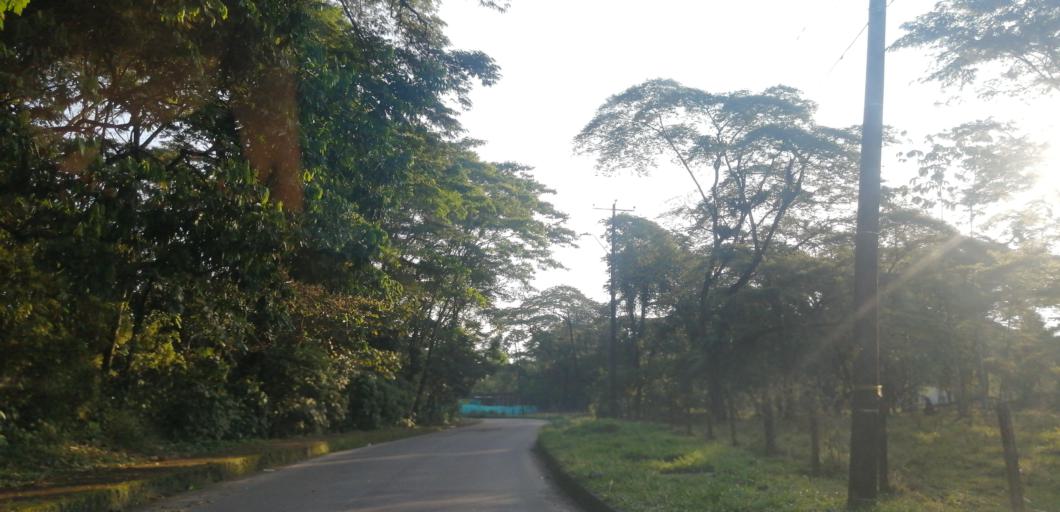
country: CO
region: Meta
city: Acacias
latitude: 3.9779
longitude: -73.7591
